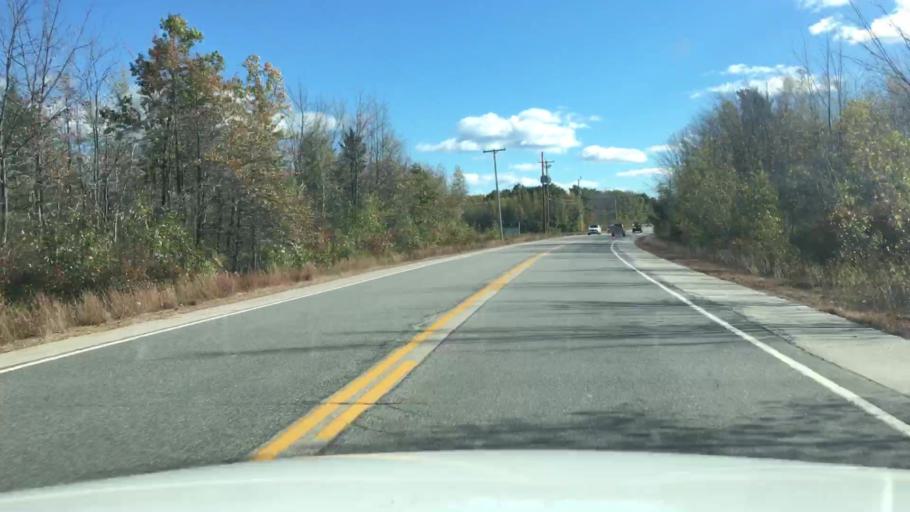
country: US
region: Maine
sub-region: York County
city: South Sanford
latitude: 43.3936
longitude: -70.6933
